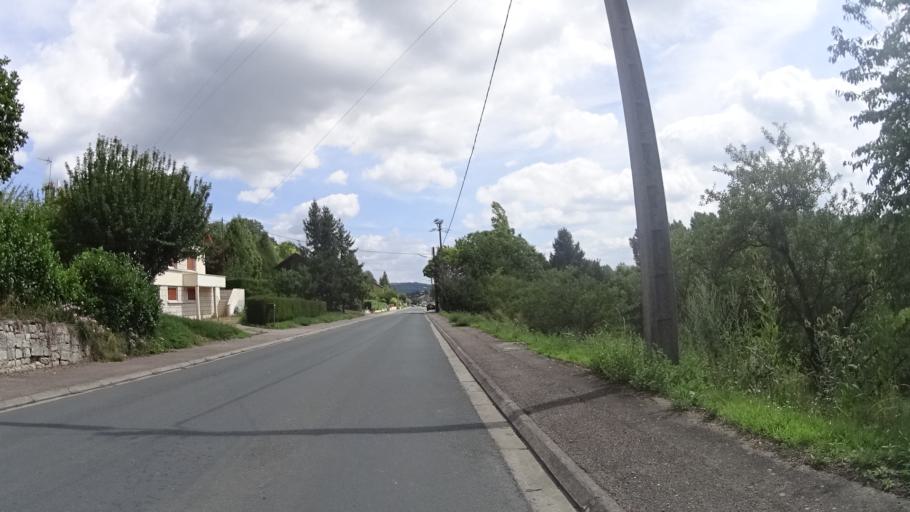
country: FR
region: Lorraine
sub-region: Departement de la Meuse
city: Euville
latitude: 48.7459
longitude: 5.6302
